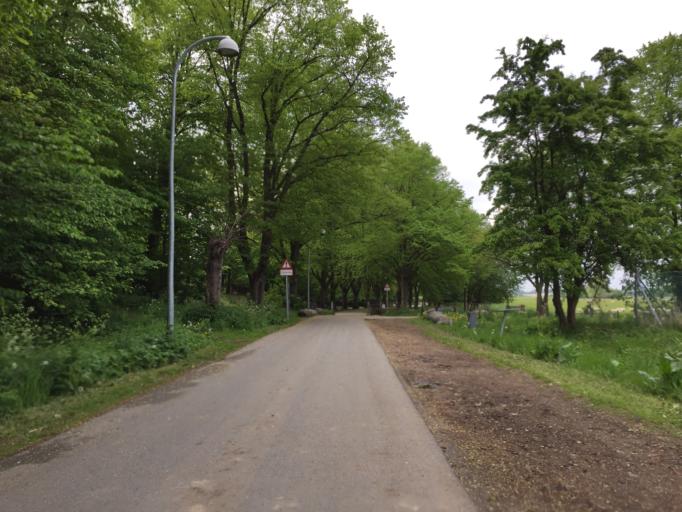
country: DK
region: Capital Region
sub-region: Brondby Kommune
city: Brondbyvester
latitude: 55.6292
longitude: 12.4378
